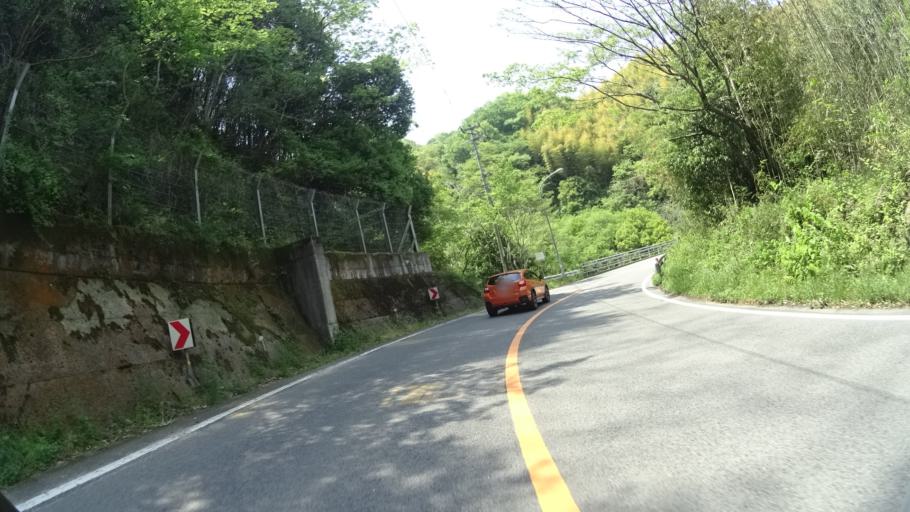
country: JP
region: Ehime
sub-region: Shikoku-chuo Shi
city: Matsuyama
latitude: 33.8824
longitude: 132.8360
